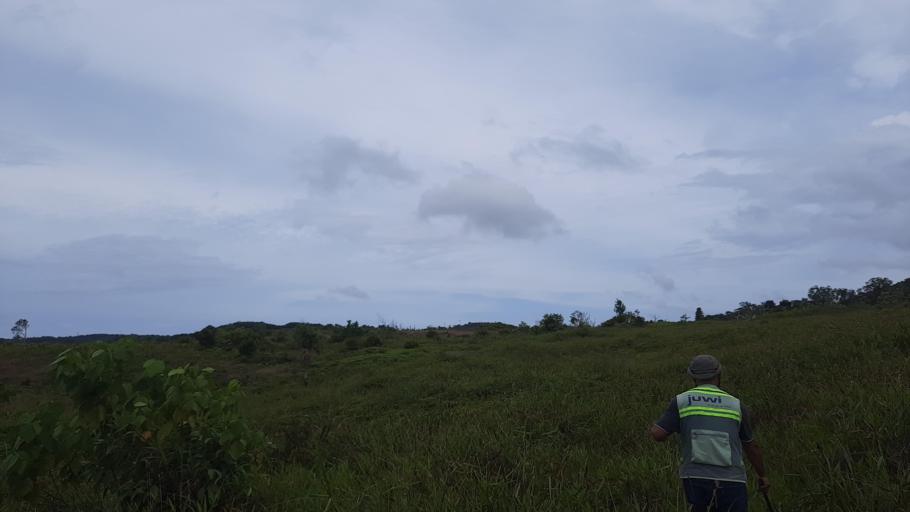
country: PW
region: Aimeliik
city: Ngchemiangel
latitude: 7.4480
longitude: 134.5366
